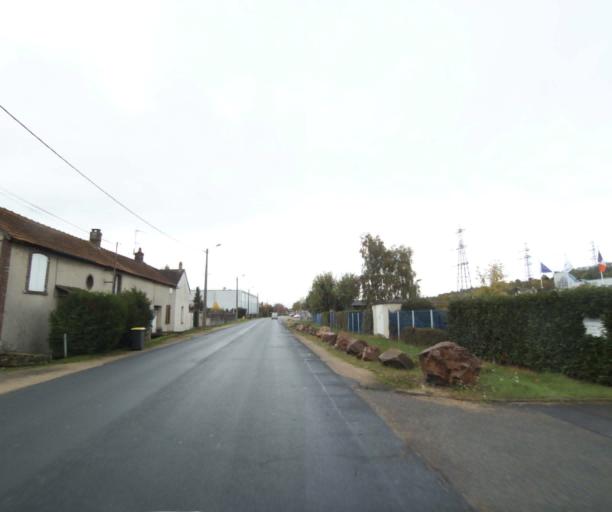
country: FR
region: Centre
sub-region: Departement d'Eure-et-Loir
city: Dreux
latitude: 48.7454
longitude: 1.3849
